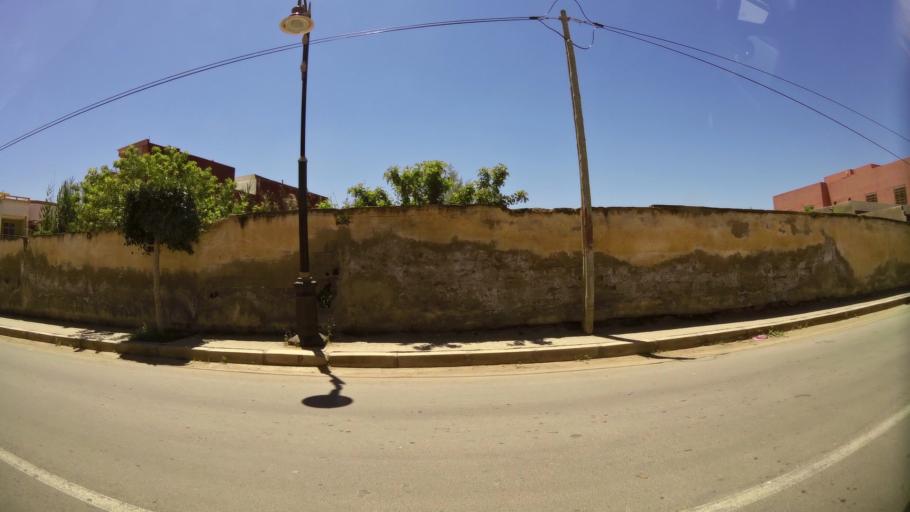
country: MA
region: Oriental
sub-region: Berkane-Taourirt
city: Madagh
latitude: 35.0817
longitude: -2.2298
